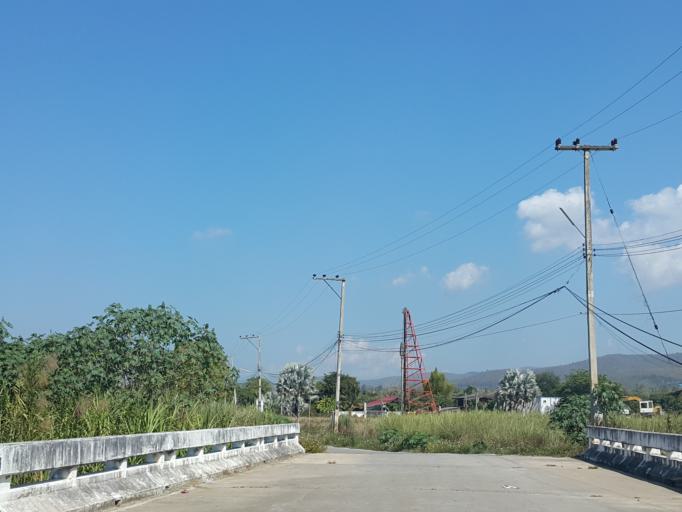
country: TH
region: Chiang Mai
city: Mae Taeng
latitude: 18.9961
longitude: 98.9833
